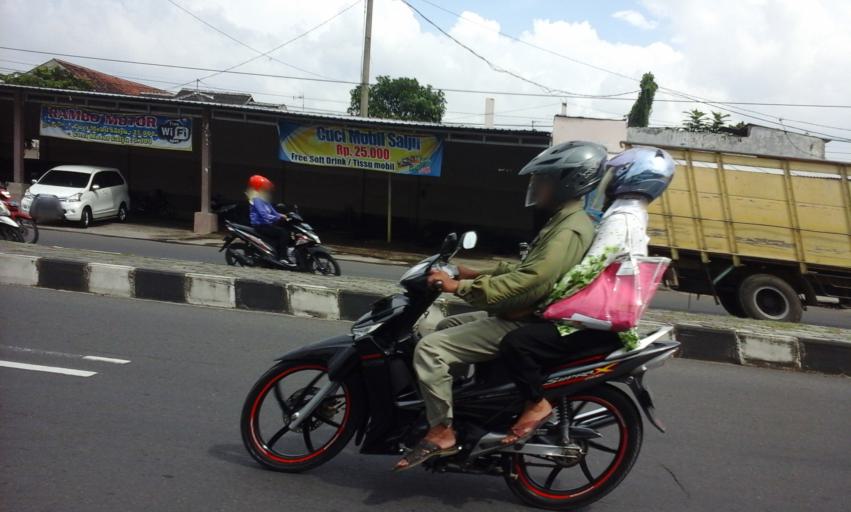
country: ID
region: East Java
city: Krajan
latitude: -8.1870
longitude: 113.6601
